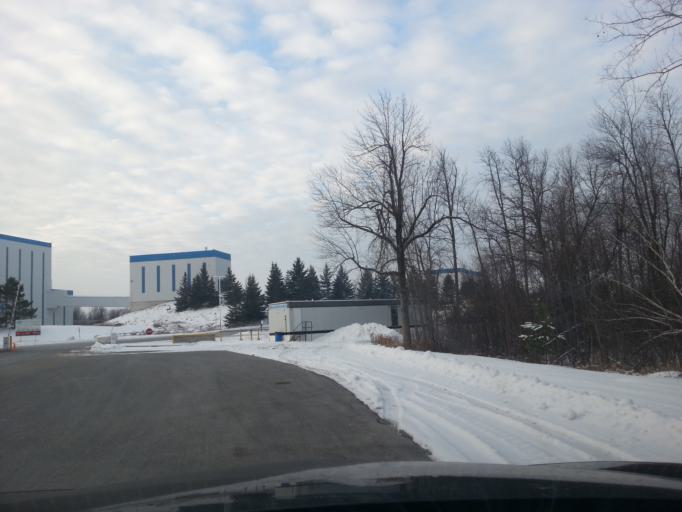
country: CA
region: Ontario
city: Perth
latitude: 44.8797
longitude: -76.3291
